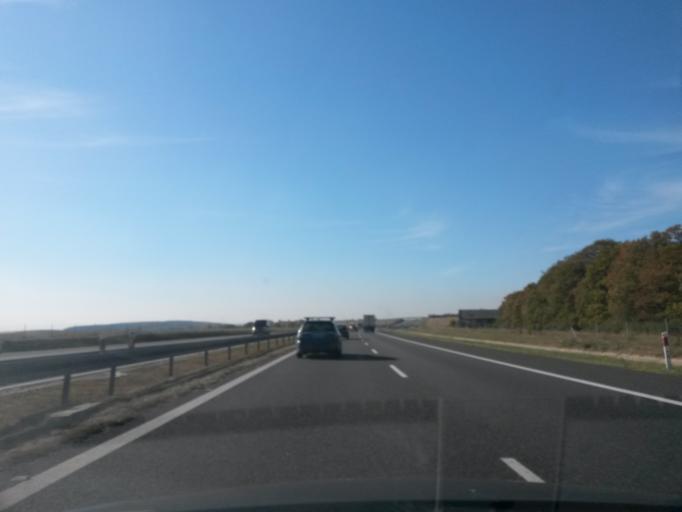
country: PL
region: Opole Voivodeship
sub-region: Powiat krapkowicki
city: Rozwadza
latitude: 50.4781
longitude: 18.0708
